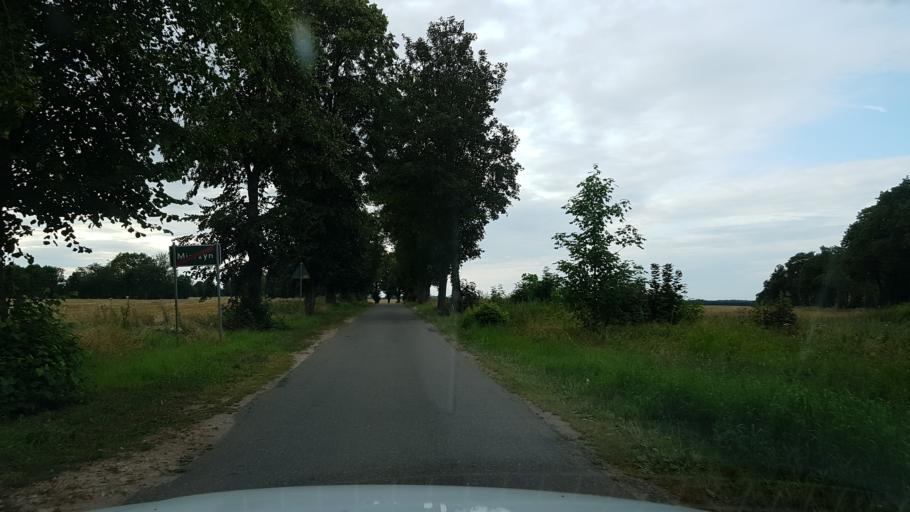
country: PL
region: West Pomeranian Voivodeship
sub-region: Powiat bialogardzki
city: Karlino
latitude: 54.1123
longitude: 15.8805
